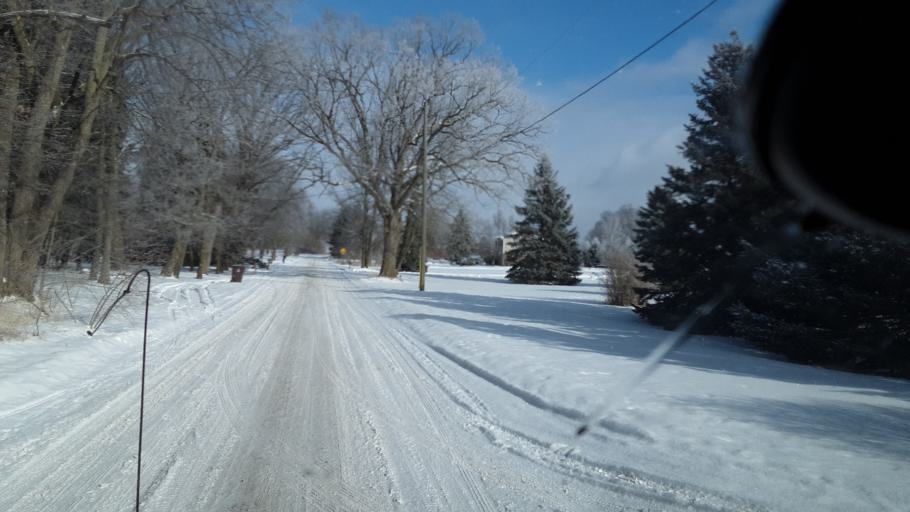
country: US
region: Michigan
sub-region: Eaton County
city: Eaton Rapids
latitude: 42.5214
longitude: -84.6309
